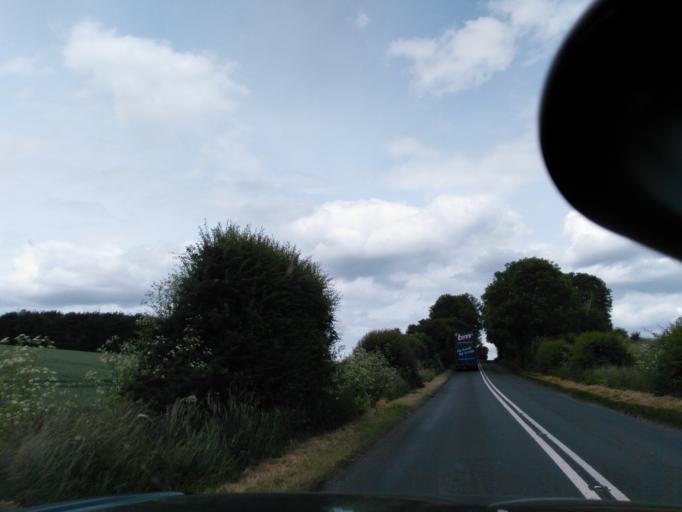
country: GB
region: England
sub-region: Wiltshire
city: Woodford
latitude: 51.1417
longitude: -1.8583
